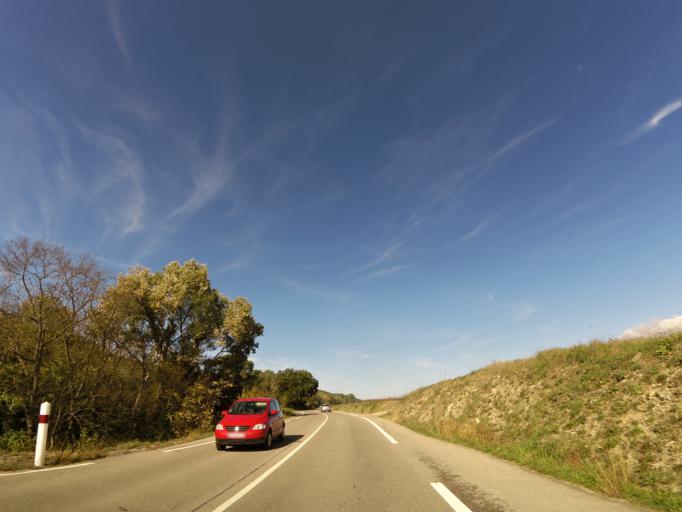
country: FR
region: Languedoc-Roussillon
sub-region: Departement du Gard
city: Ledignan
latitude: 43.9310
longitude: 4.1035
